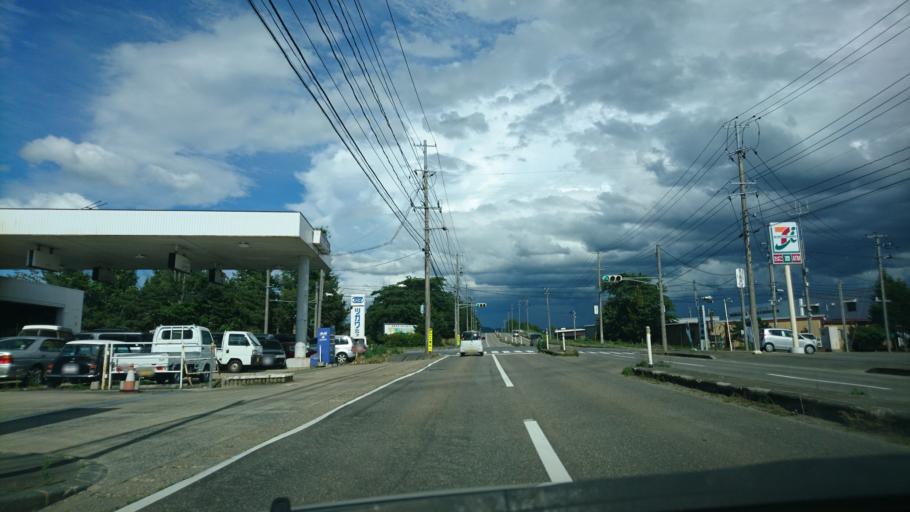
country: JP
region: Iwate
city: Hanamaki
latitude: 39.3356
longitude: 141.1165
